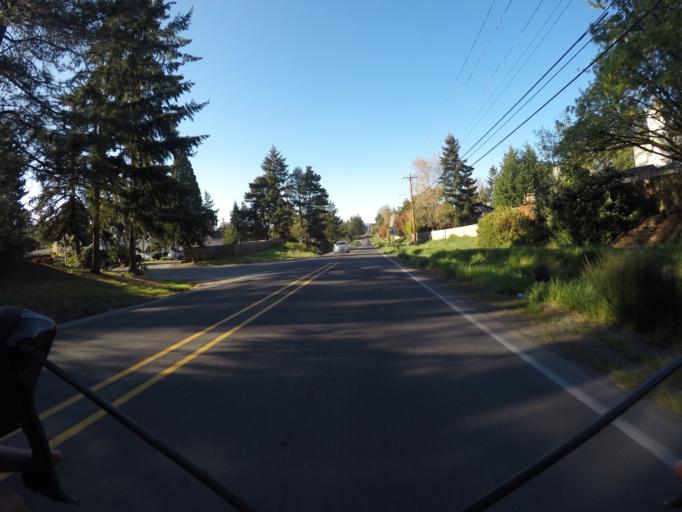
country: US
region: Oregon
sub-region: Washington County
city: Aloha
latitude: 45.4675
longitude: -122.8675
